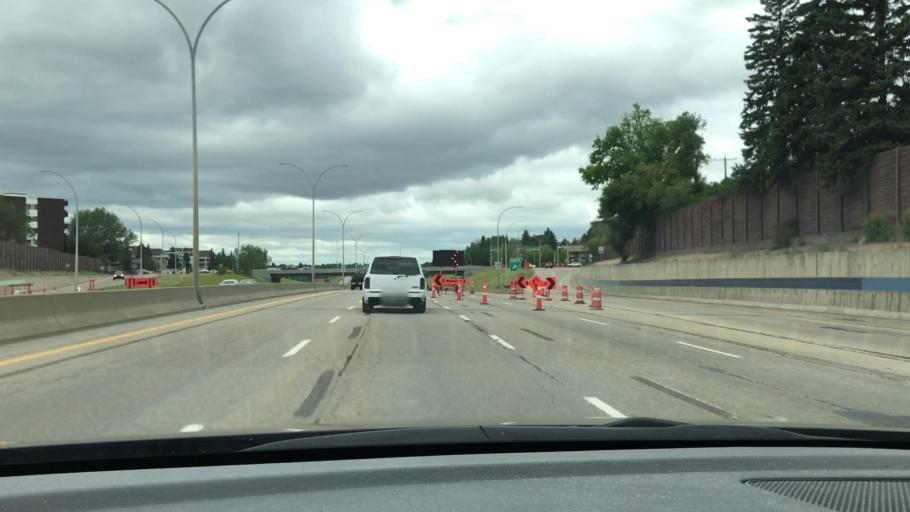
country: CA
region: Alberta
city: Edmonton
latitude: 53.4832
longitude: -113.5371
